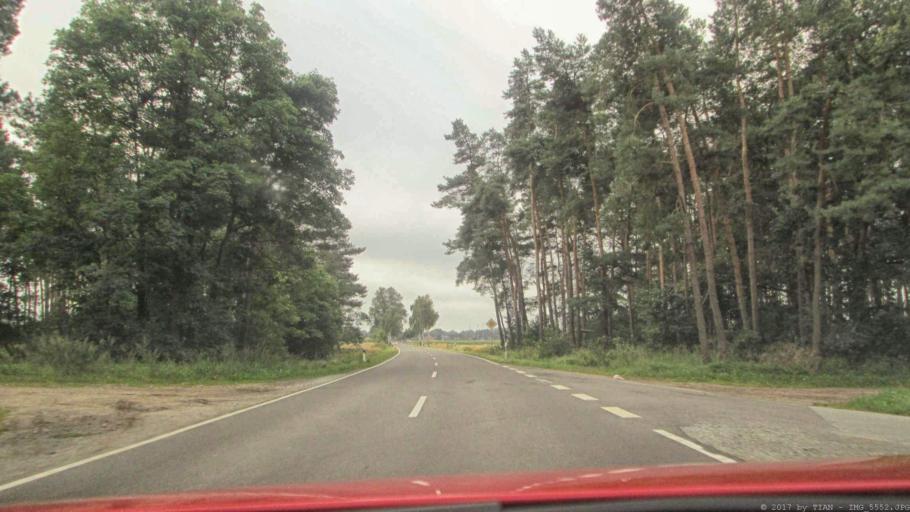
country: DE
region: Lower Saxony
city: Barwedel
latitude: 52.5801
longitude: 10.7873
